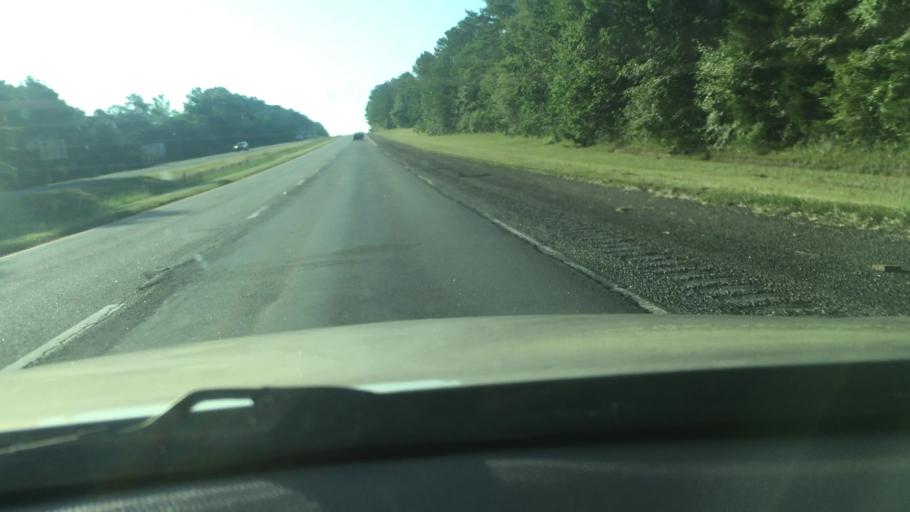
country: US
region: South Carolina
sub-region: Richland County
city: Lake Murray of Richland
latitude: 34.1576
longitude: -81.2679
